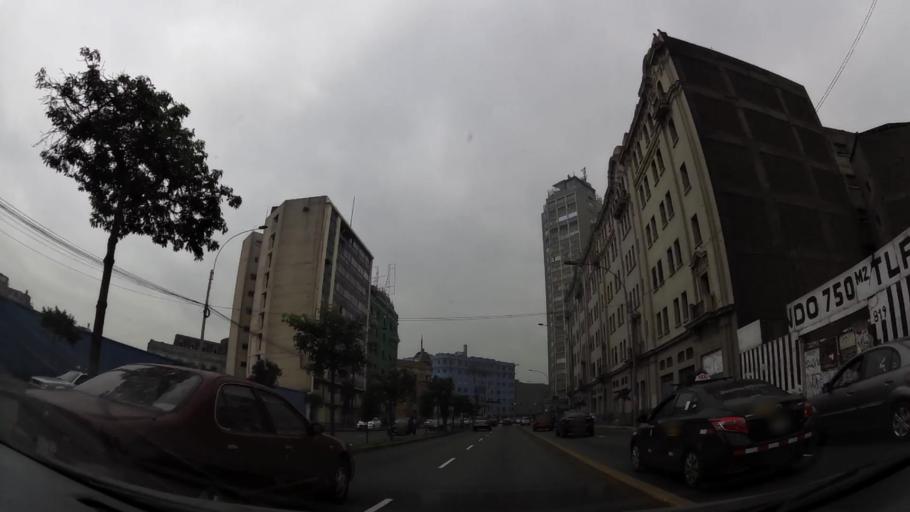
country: PE
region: Lima
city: Lima
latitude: -12.0499
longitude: -77.0388
